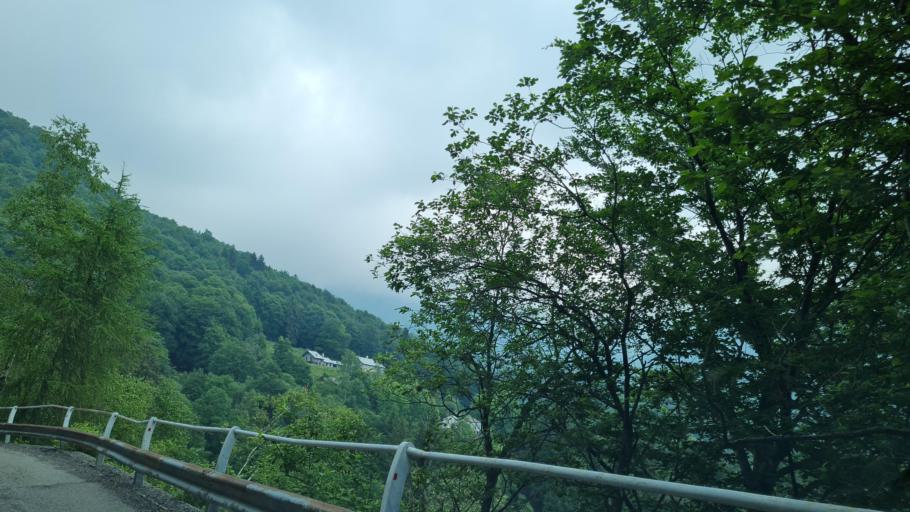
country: IT
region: Piedmont
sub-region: Provincia di Biella
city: San Paolo Cervo
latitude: 45.6188
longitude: 7.9800
